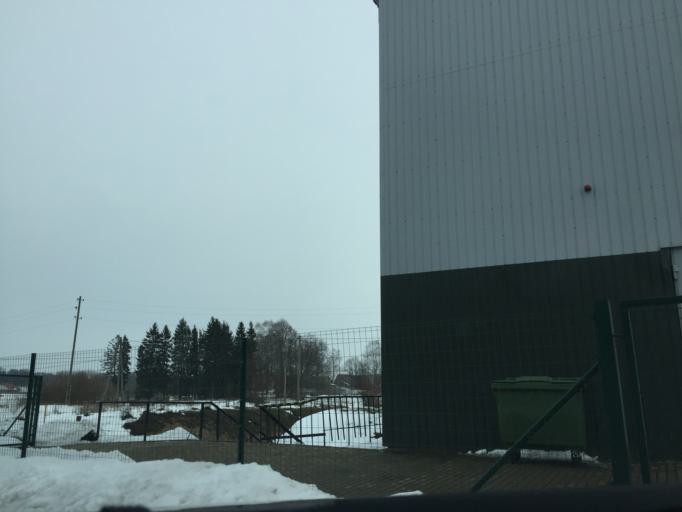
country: LV
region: Ikskile
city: Ikskile
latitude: 56.8423
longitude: 24.4593
